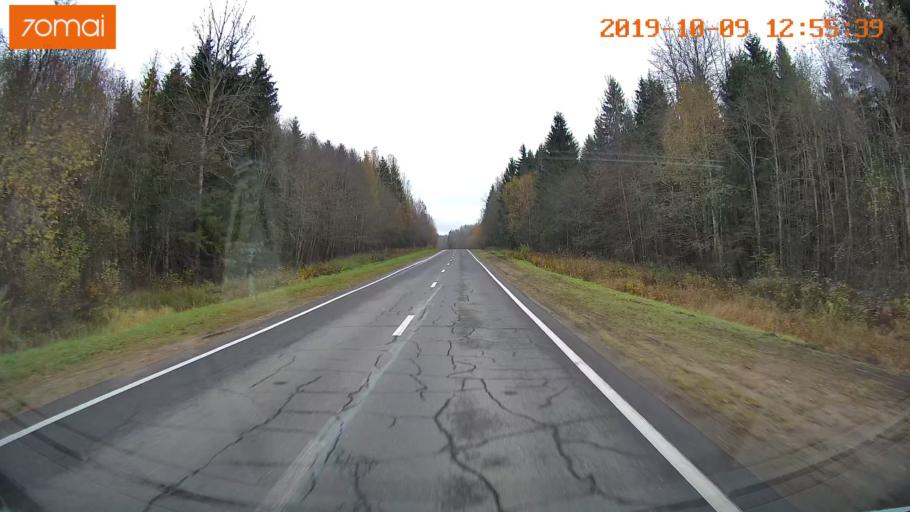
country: RU
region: Jaroslavl
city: Prechistoye
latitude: 58.3984
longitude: 40.3989
